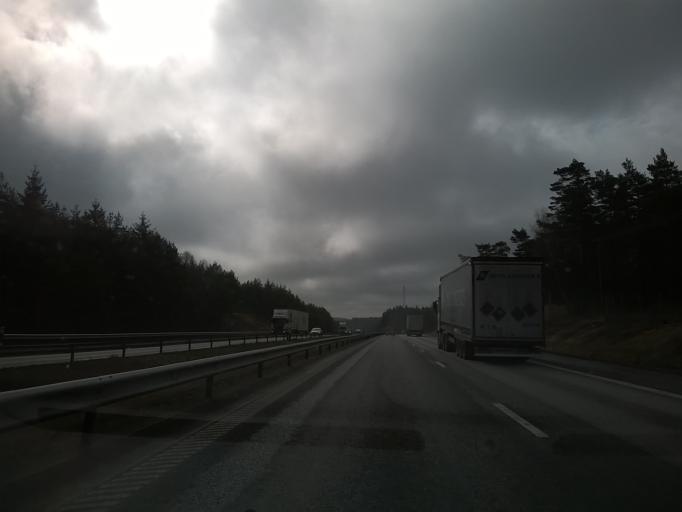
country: SE
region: Halland
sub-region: Varbergs Kommun
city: Varberg
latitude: 57.1953
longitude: 12.2528
